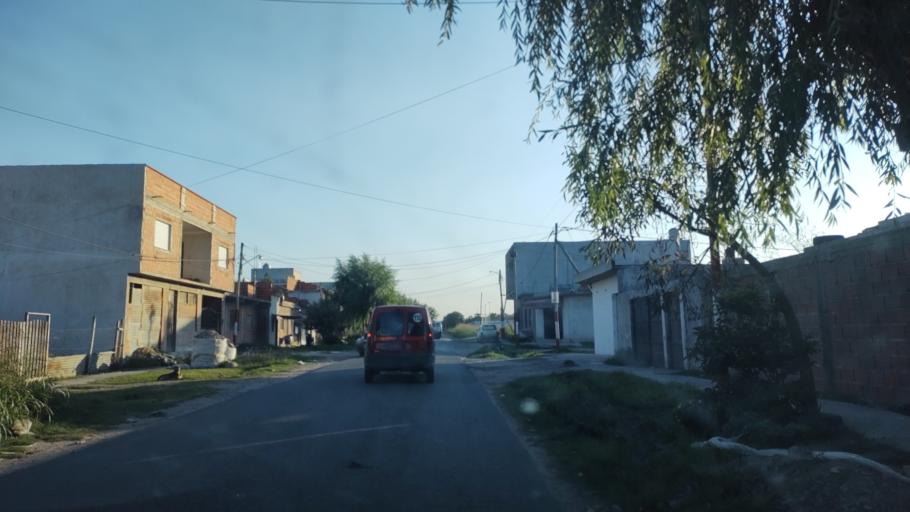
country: AR
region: Buenos Aires
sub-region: Partido de La Plata
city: La Plata
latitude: -34.9682
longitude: -57.9686
